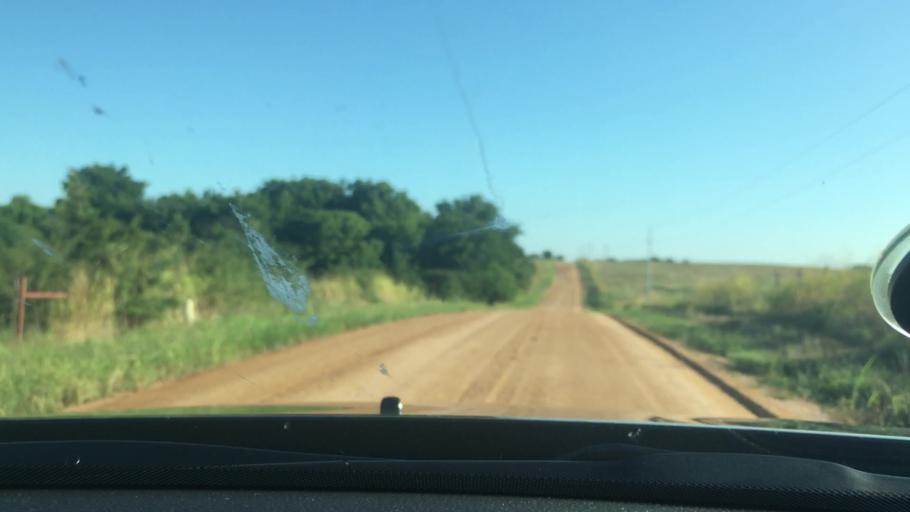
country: US
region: Oklahoma
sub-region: Murray County
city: Sulphur
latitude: 34.4139
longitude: -96.7936
